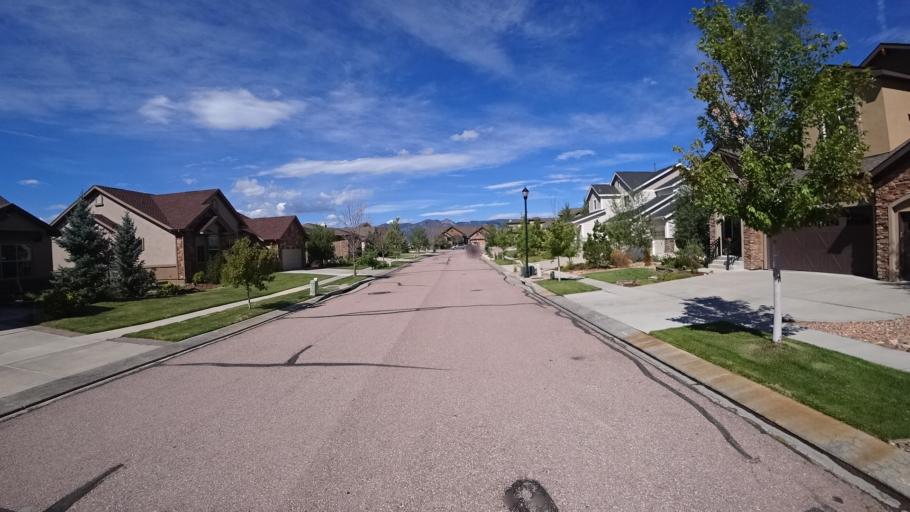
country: US
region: Colorado
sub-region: El Paso County
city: Gleneagle
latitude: 39.0249
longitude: -104.8061
